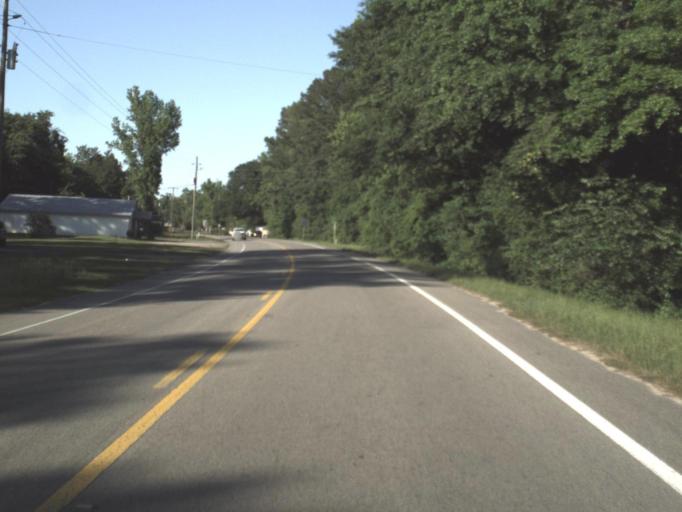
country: US
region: Florida
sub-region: Liberty County
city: Bristol
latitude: 30.3765
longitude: -84.8025
